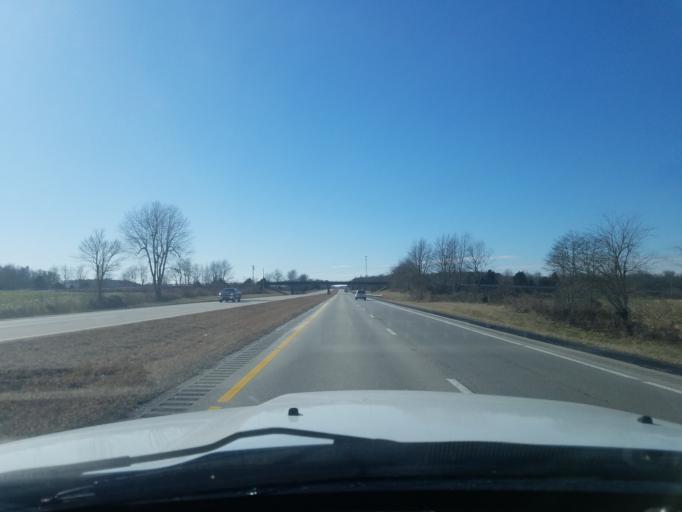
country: US
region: Kentucky
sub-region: Hardin County
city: Elizabethtown
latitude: 37.6208
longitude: -85.9524
